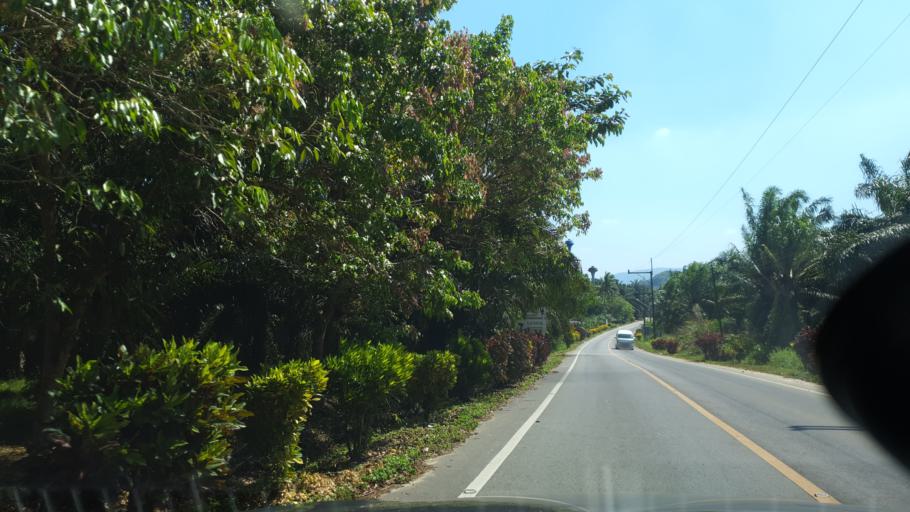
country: TH
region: Krabi
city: Khlong Thom
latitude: 7.9390
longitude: 99.2176
